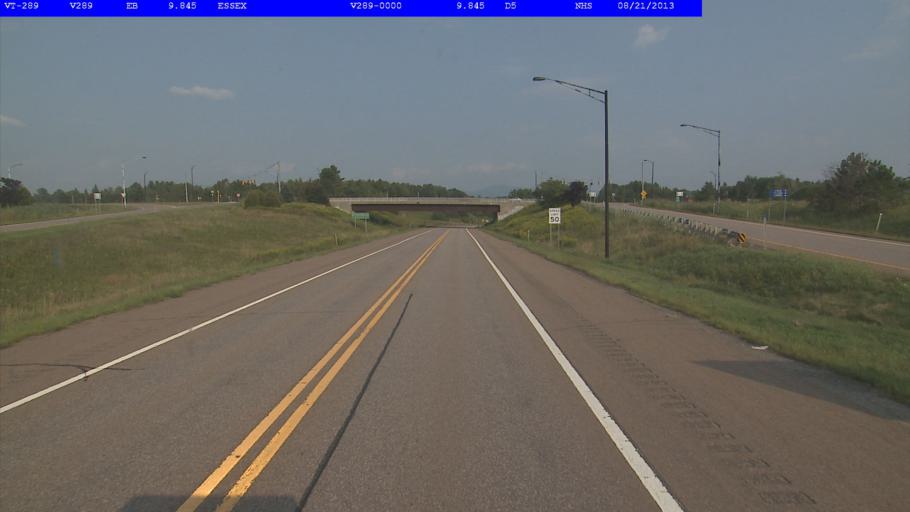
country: US
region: Vermont
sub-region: Chittenden County
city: Essex Junction
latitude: 44.5050
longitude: -73.0812
